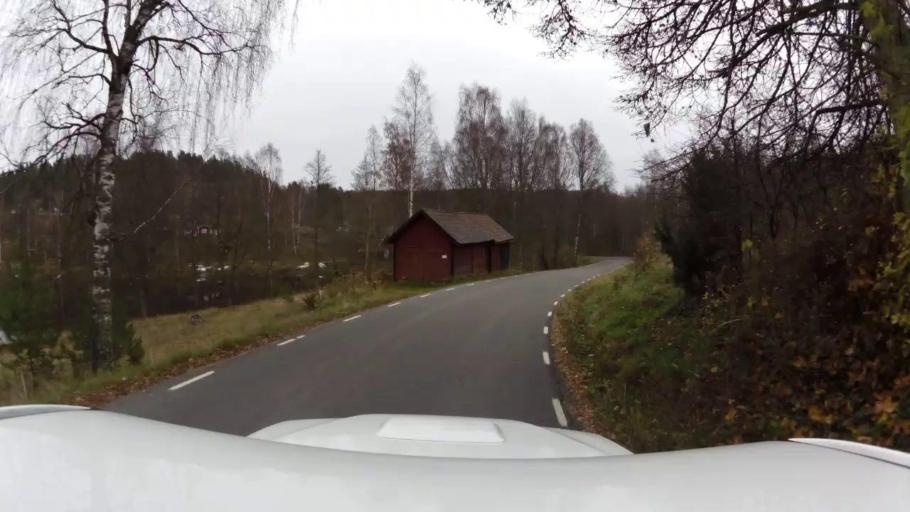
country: SE
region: OEstergoetland
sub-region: Kinda Kommun
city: Rimforsa
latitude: 58.1378
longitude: 15.6056
